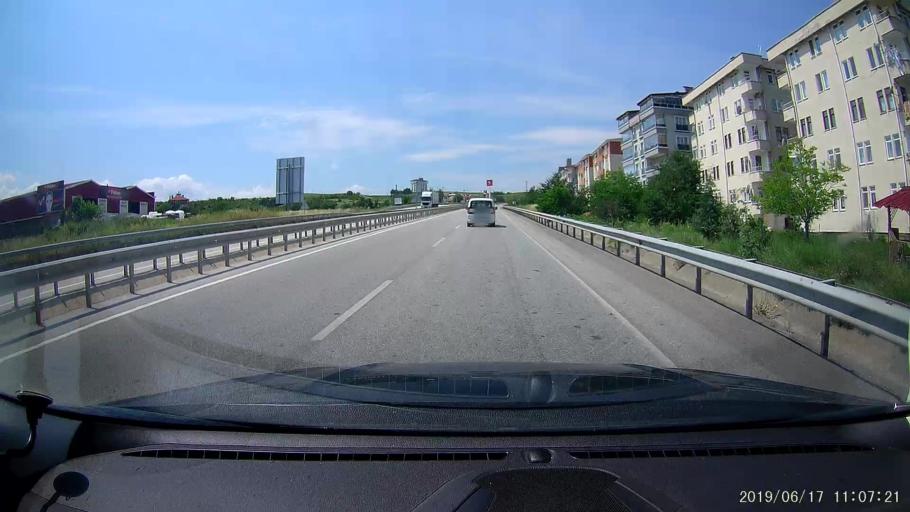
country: TR
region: Kastamonu
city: Tosya
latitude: 41.0036
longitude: 34.0553
